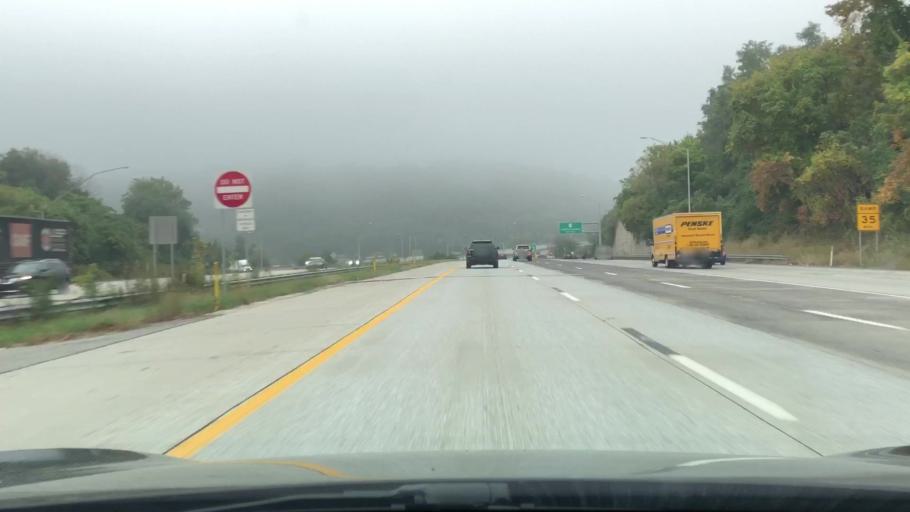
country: US
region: Pennsylvania
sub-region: Montgomery County
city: West Conshohocken
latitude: 40.0697
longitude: -75.3219
